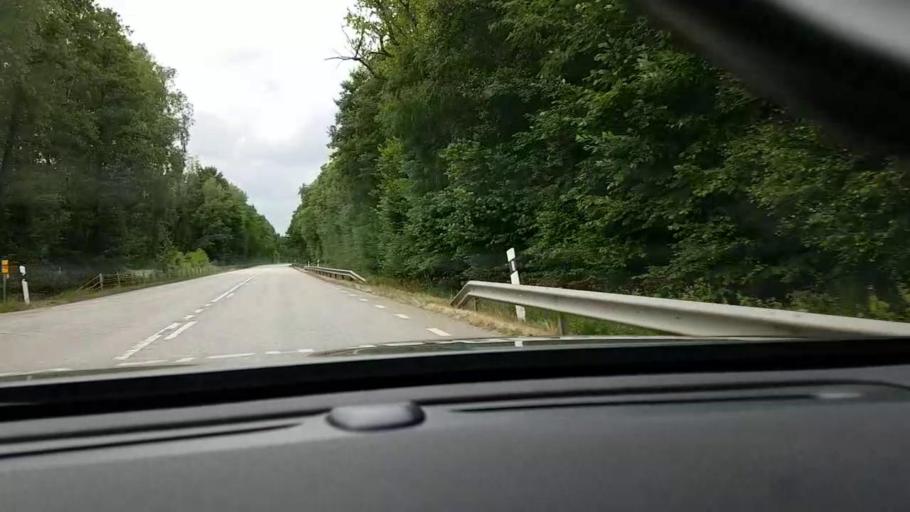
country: SE
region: Skane
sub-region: Horby Kommun
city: Hoerby
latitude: 55.8699
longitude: 13.6363
